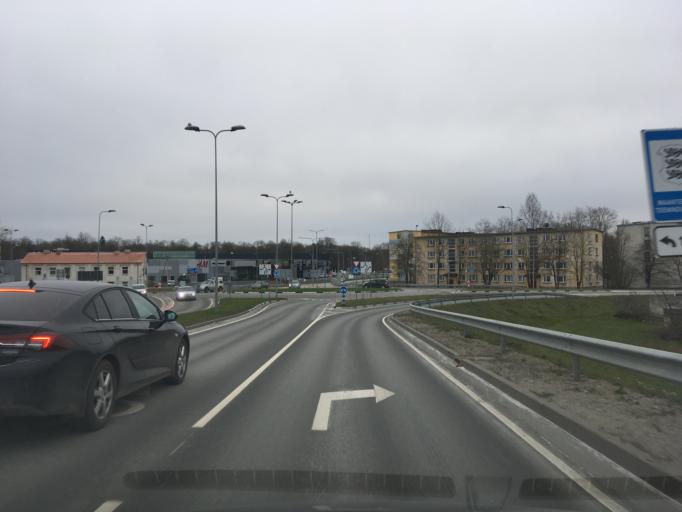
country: EE
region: Ida-Virumaa
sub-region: Johvi vald
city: Johvi
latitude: 59.3548
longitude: 27.4156
